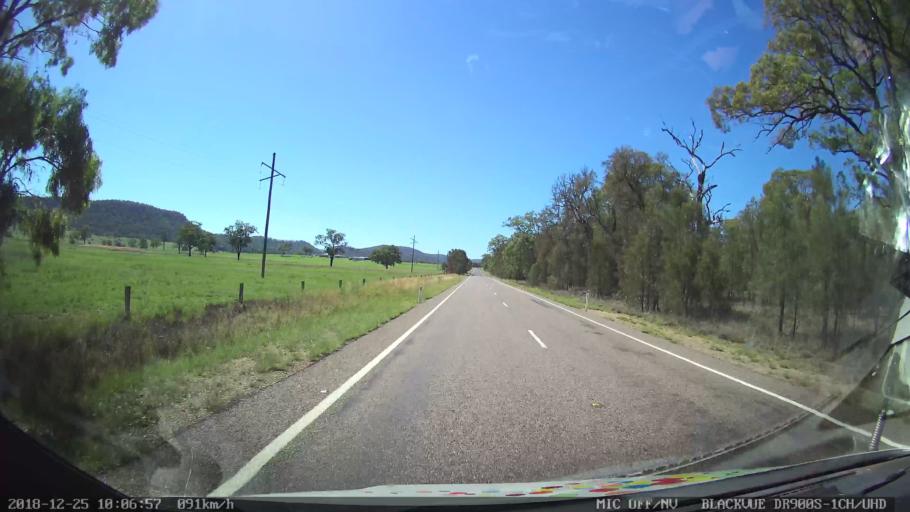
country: AU
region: New South Wales
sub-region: Upper Hunter Shire
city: Merriwa
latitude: -32.2656
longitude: 150.4940
